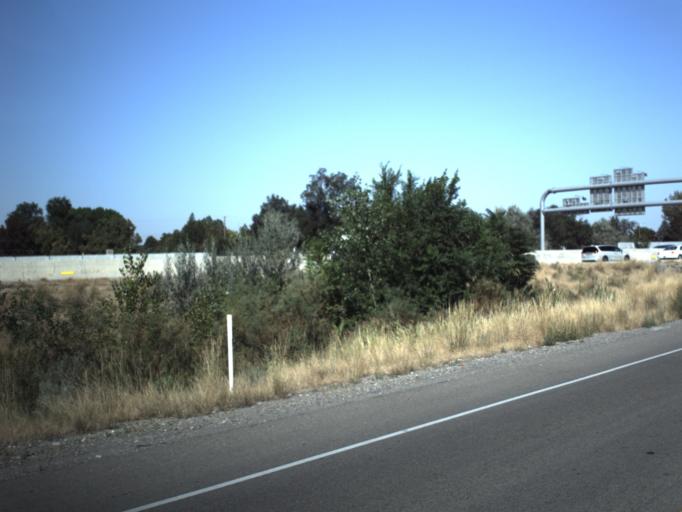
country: US
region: Utah
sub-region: Salt Lake County
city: Salt Lake City
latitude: 40.7963
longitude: -111.9171
